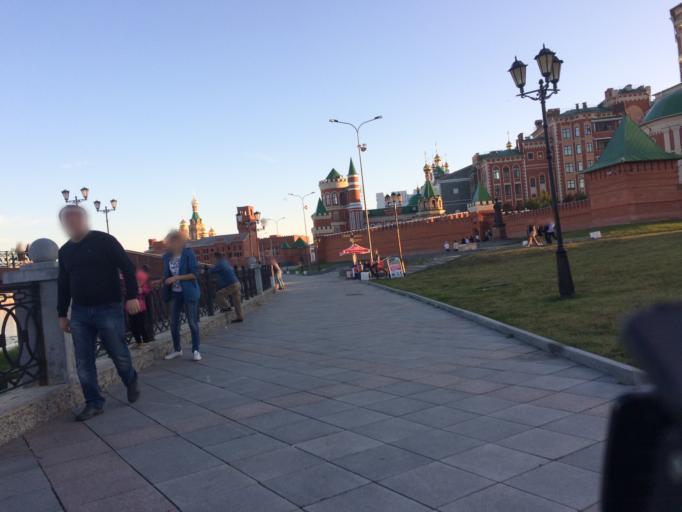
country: RU
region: Mariy-El
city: Yoshkar-Ola
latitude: 56.6376
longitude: 47.9040
